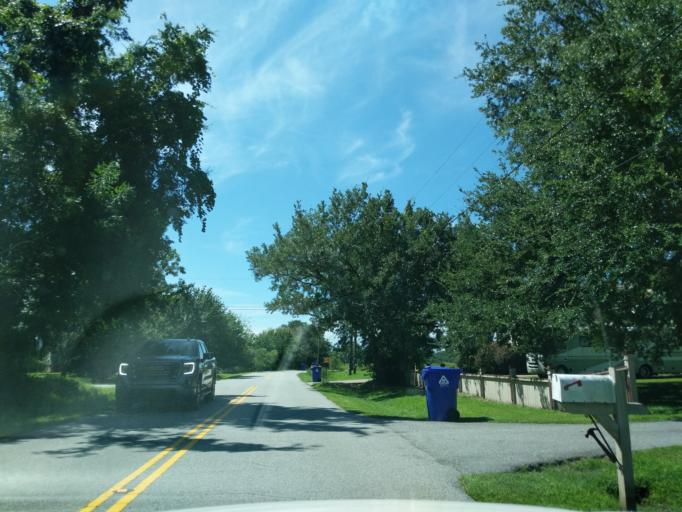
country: US
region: South Carolina
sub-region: Charleston County
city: Folly Beach
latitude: 32.6955
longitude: -79.9579
